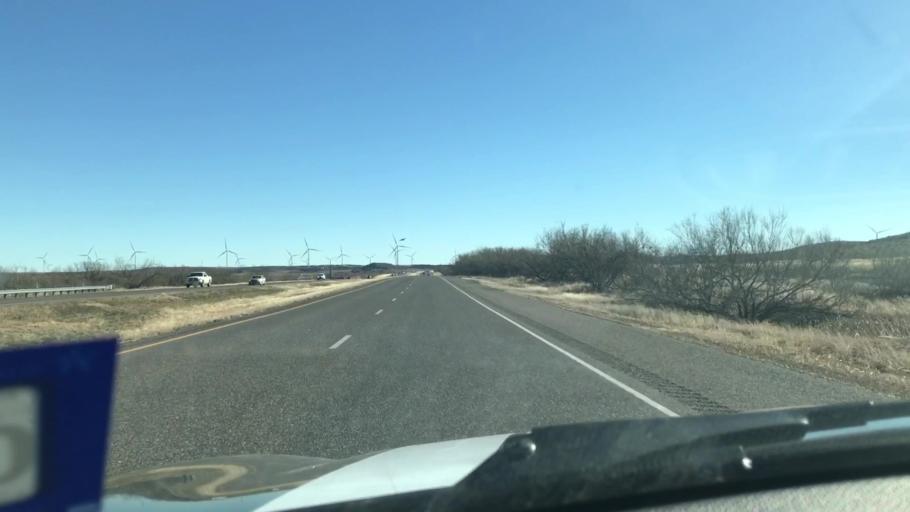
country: US
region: Texas
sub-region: Scurry County
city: Snyder
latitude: 32.9318
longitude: -101.0703
